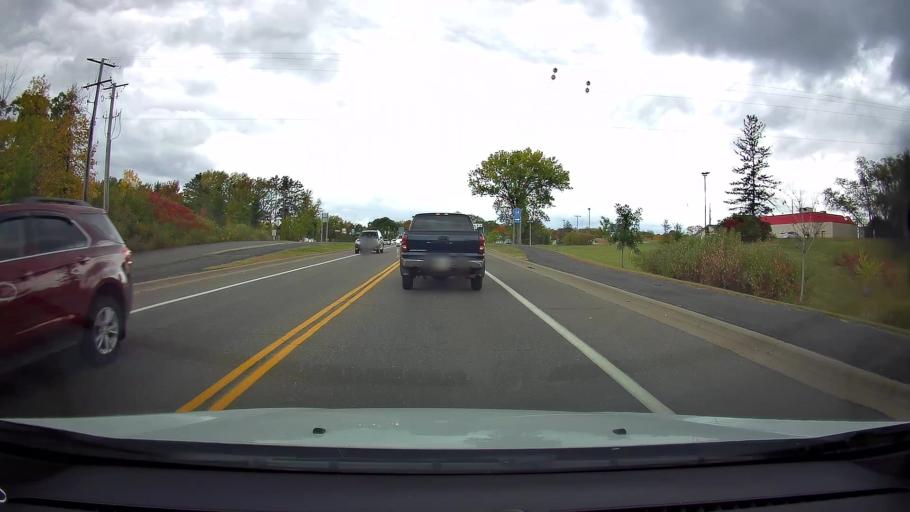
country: US
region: Minnesota
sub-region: Chisago County
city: Lindstrom
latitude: 45.3910
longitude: -92.8539
